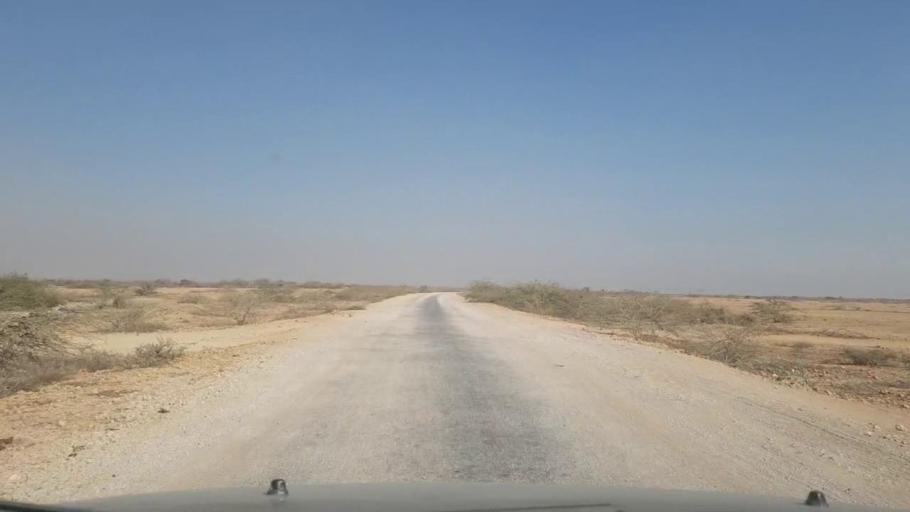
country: PK
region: Sindh
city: Thatta
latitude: 24.9019
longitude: 67.9220
